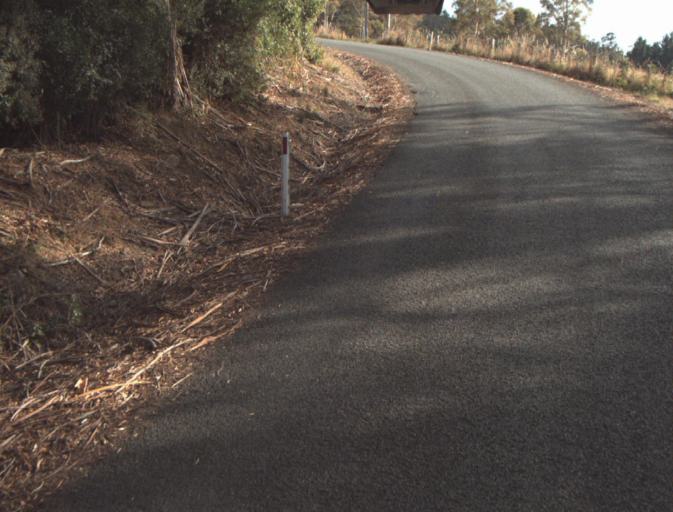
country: AU
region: Tasmania
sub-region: Launceston
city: Mayfield
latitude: -41.2884
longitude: 147.2070
